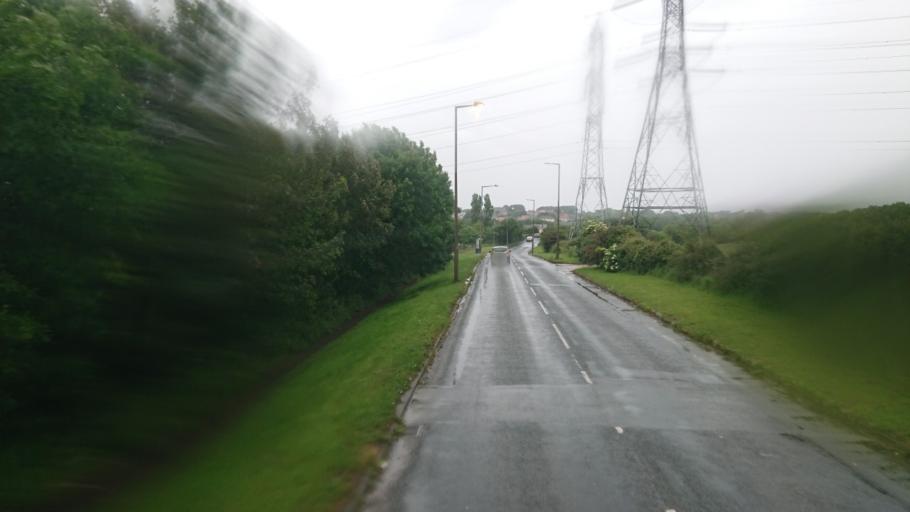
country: GB
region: England
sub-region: Lancashire
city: Morecambe
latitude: 54.0312
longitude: -2.8956
